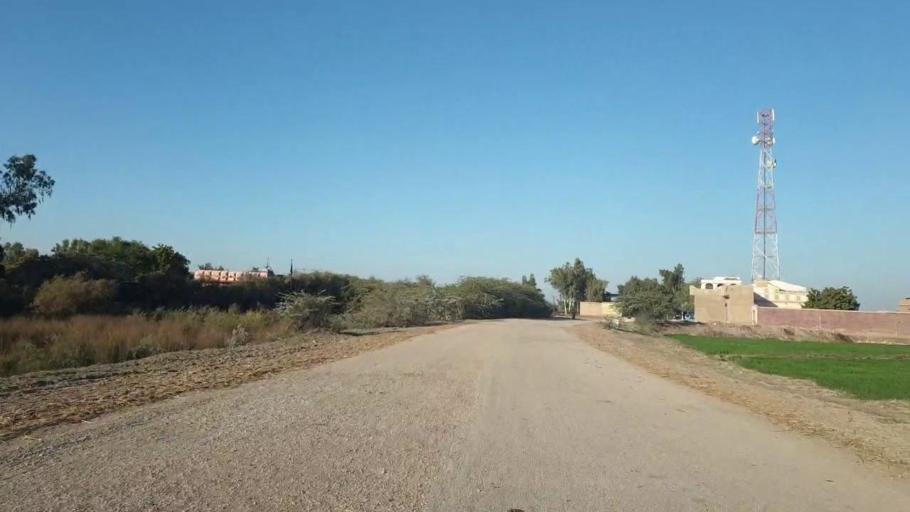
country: PK
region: Sindh
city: Dokri
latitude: 27.3669
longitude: 68.1160
